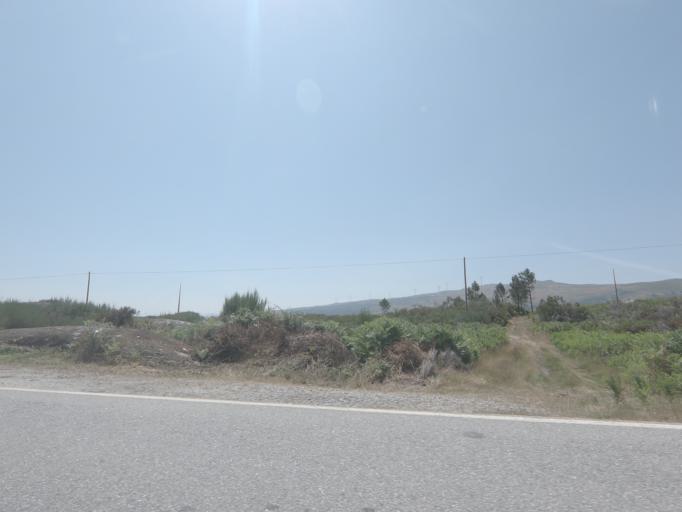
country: PT
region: Viseu
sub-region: Castro Daire
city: Castro Daire
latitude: 40.9689
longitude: -7.8839
